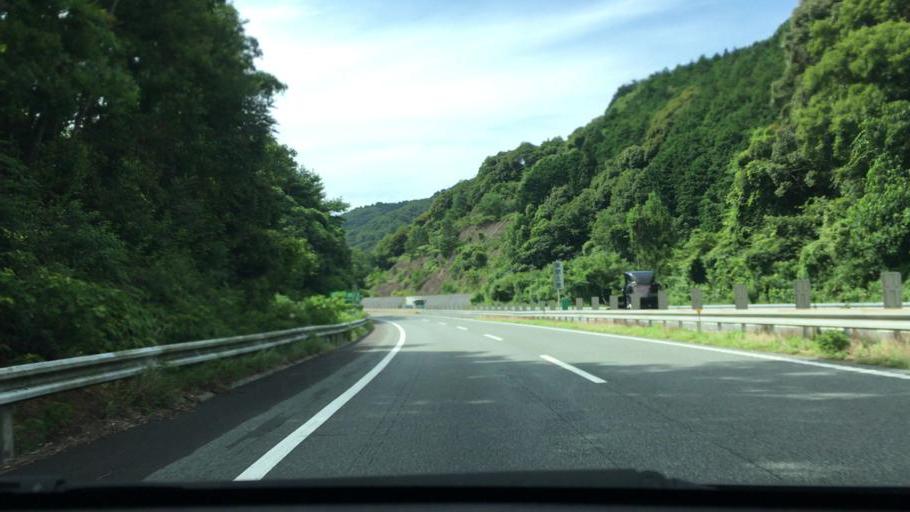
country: JP
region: Yamaguchi
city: Ogori-shimogo
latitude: 34.1345
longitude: 131.3751
